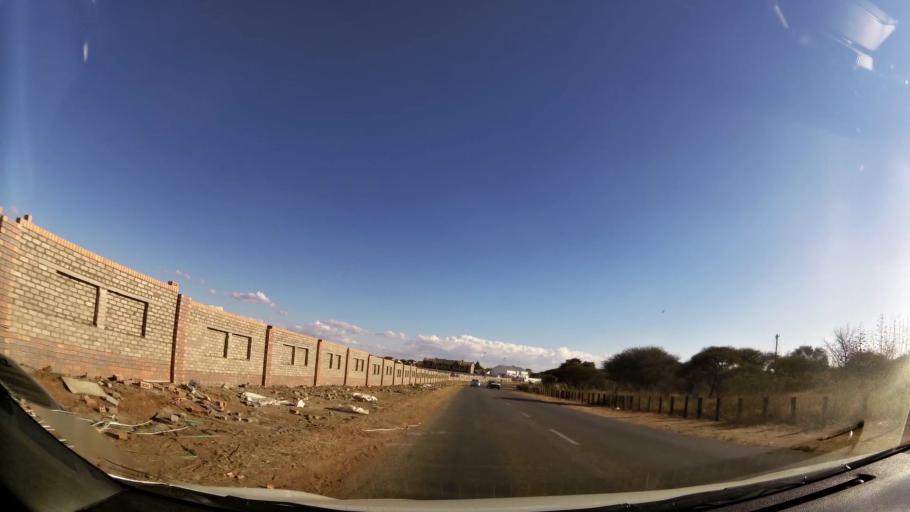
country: ZA
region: Limpopo
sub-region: Capricorn District Municipality
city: Polokwane
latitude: -23.8779
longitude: 29.4760
